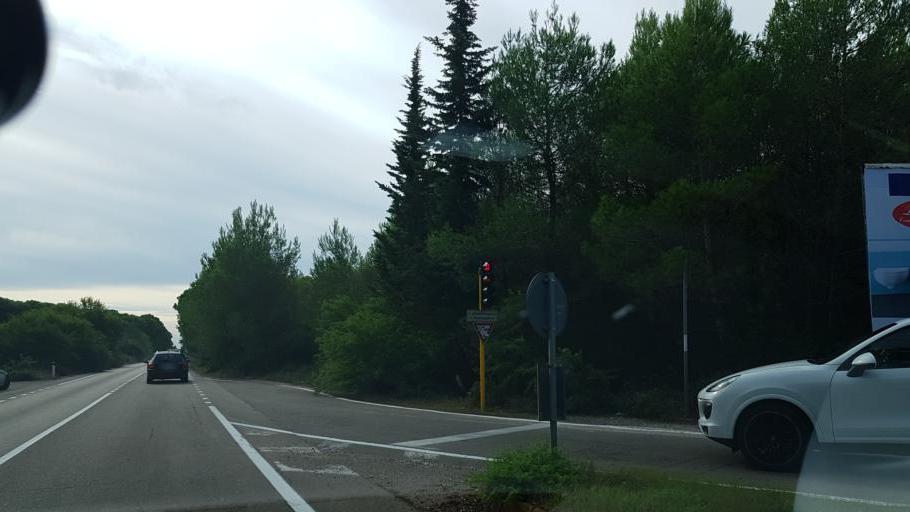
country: IT
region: Apulia
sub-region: Provincia di Lecce
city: Struda
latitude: 40.3681
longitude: 18.3102
